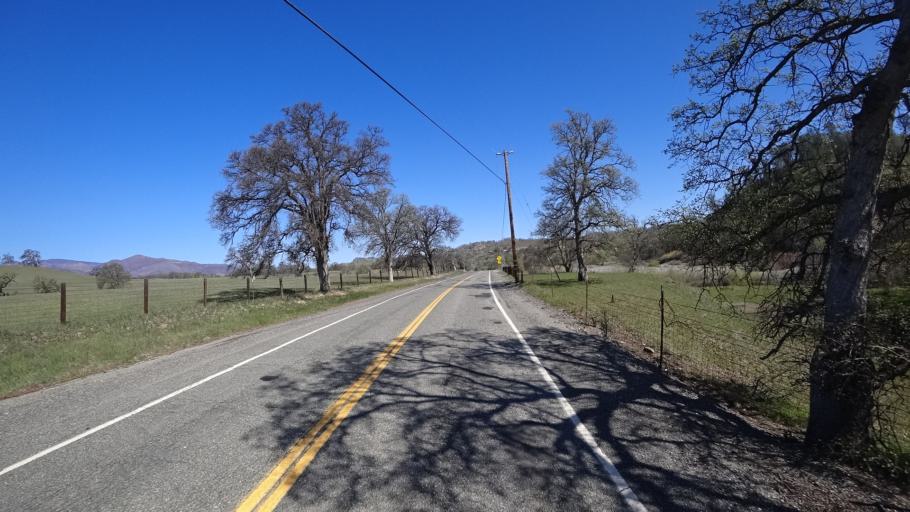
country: US
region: California
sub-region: Glenn County
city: Orland
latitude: 39.6665
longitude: -122.5257
